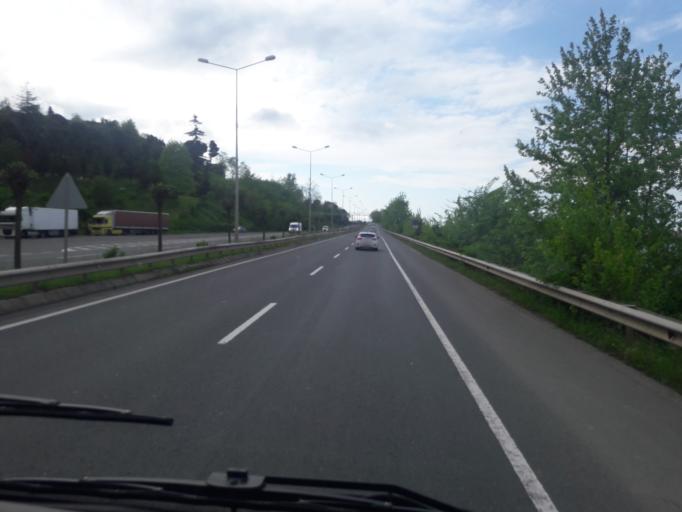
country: TR
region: Giresun
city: Piraziz
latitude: 40.9587
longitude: 38.1092
